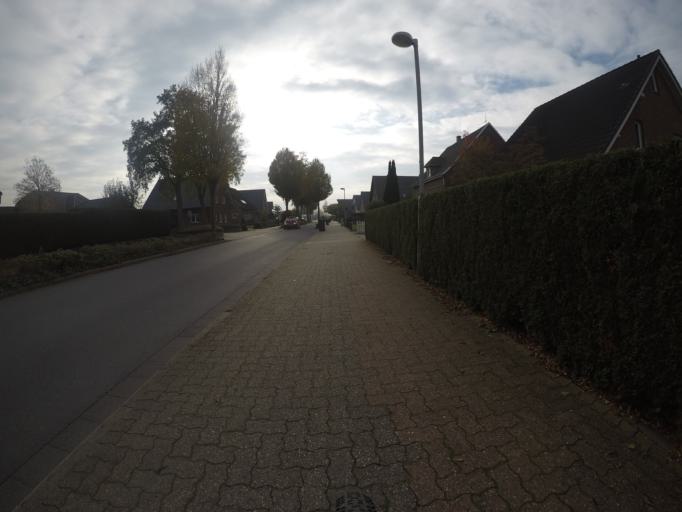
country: DE
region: North Rhine-Westphalia
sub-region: Regierungsbezirk Dusseldorf
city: Bocholt
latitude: 51.8325
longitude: 6.5756
